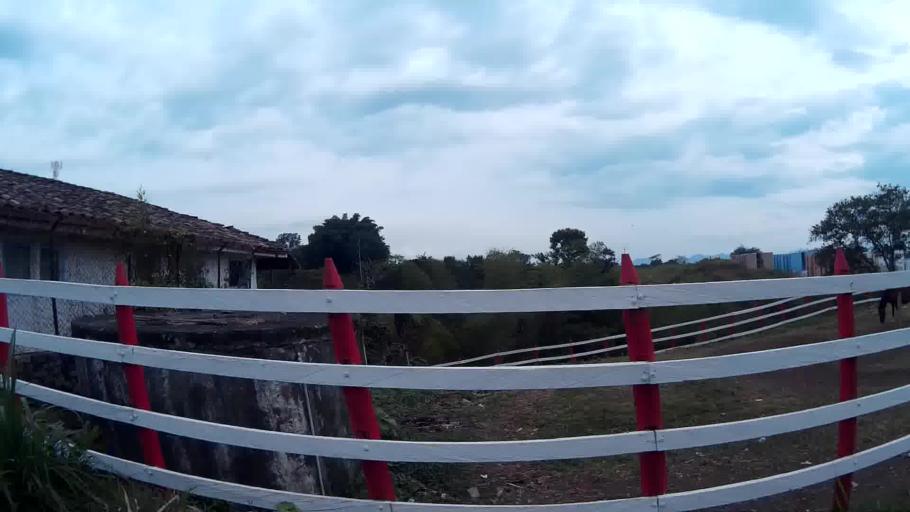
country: CO
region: Risaralda
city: Pereira
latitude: 4.7879
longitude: -75.7295
